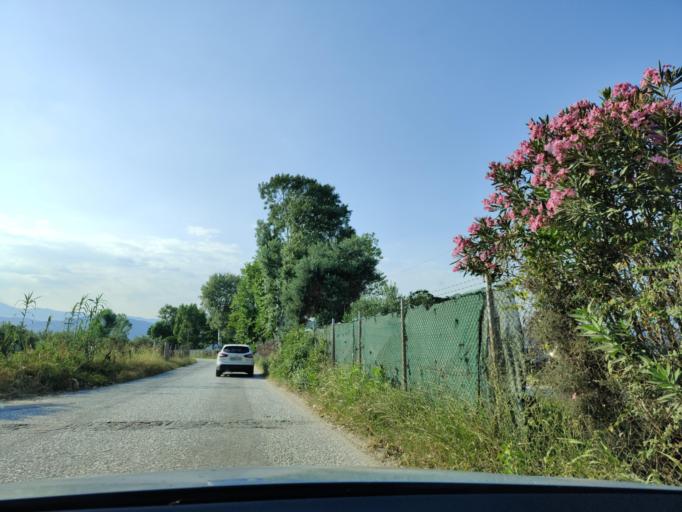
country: GR
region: East Macedonia and Thrace
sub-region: Nomos Kavalas
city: Nea Peramos
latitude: 40.8266
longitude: 24.3070
